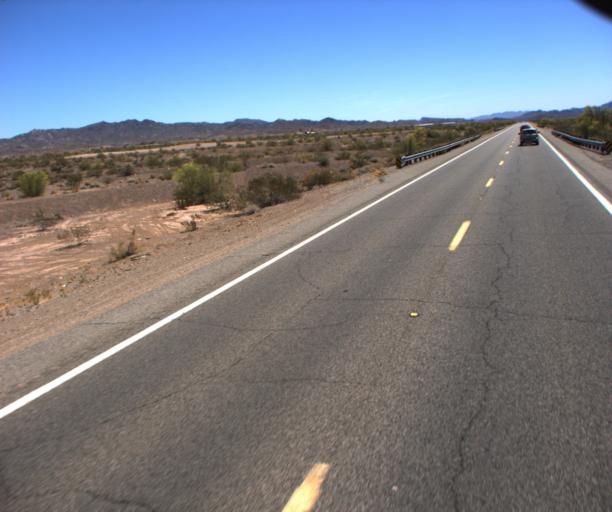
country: US
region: Arizona
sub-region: Mohave County
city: Lake Havasu City
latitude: 34.4220
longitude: -114.2027
